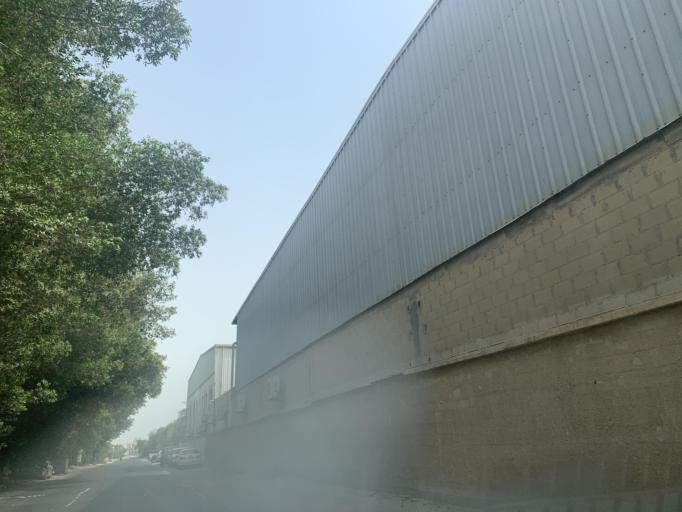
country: BH
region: Manama
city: Jidd Hafs
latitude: 26.2025
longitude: 50.4620
